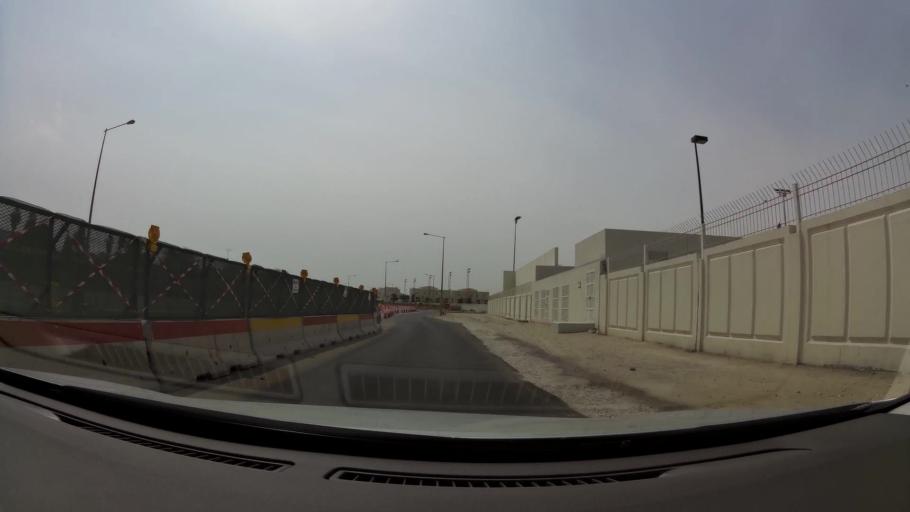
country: QA
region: Baladiyat ad Dawhah
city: Doha
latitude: 25.2631
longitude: 51.4837
